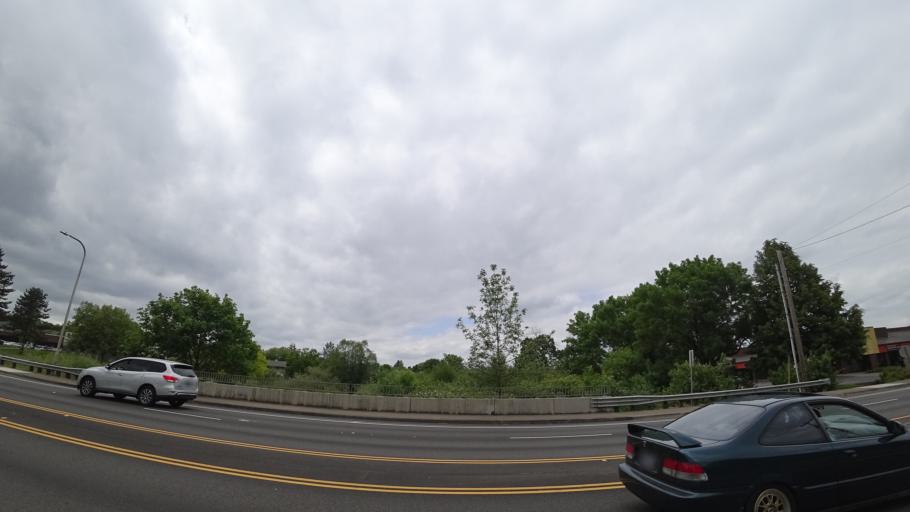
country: US
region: Oregon
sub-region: Washington County
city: Tigard
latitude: 45.4464
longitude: -122.7920
